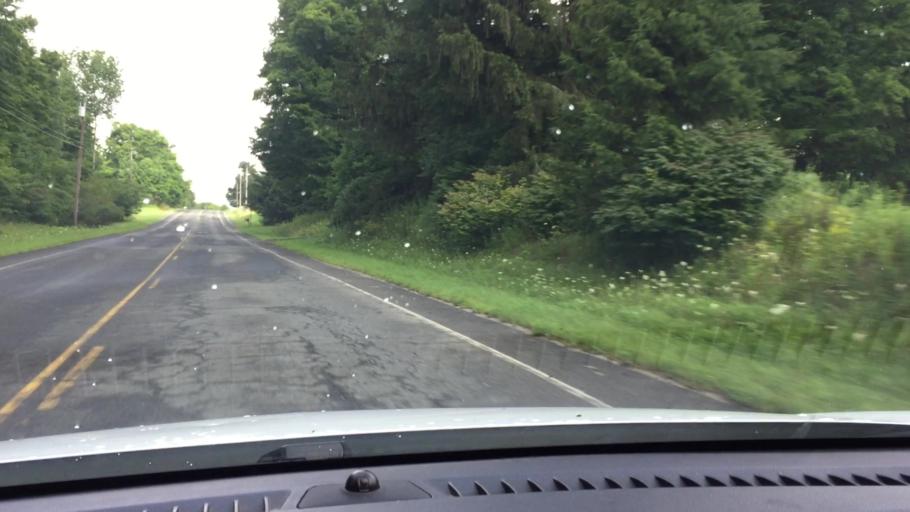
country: US
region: Massachusetts
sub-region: Berkshire County
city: Hinsdale
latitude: 42.4304
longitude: -73.0107
